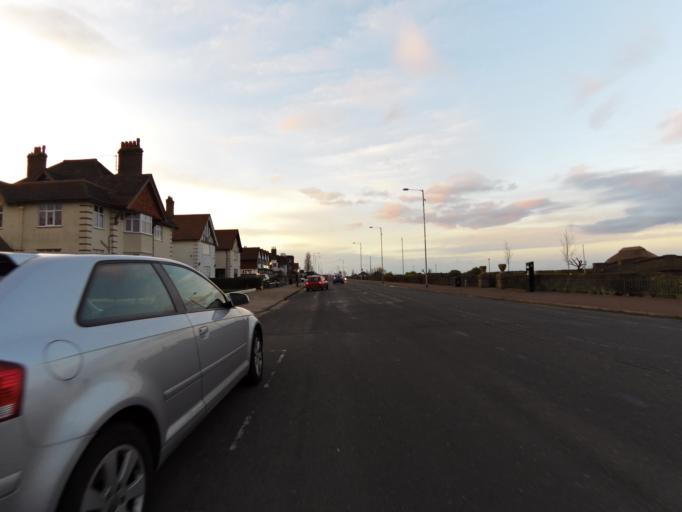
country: GB
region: England
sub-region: Norfolk
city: Great Yarmouth
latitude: 52.6150
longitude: 1.7379
